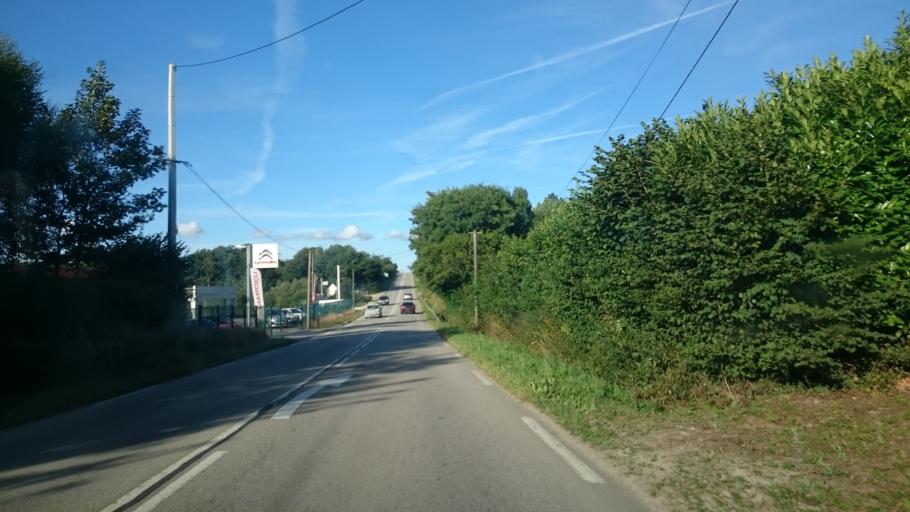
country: FR
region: Lower Normandy
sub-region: Departement de la Manche
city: Martinvast
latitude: 49.5747
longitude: -1.7149
